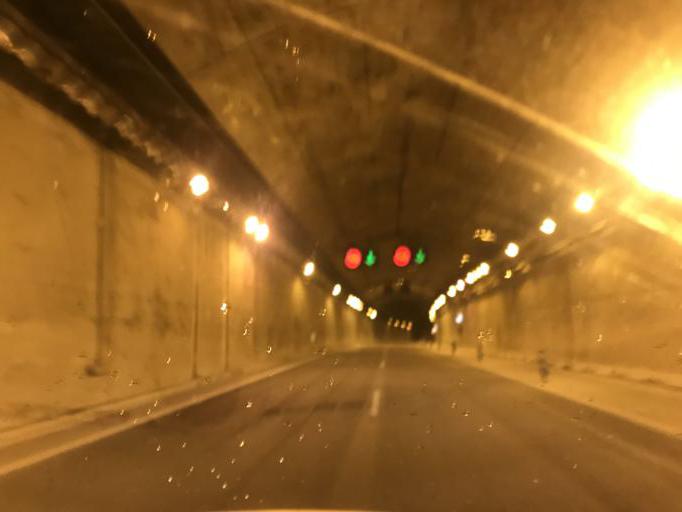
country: ES
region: Madrid
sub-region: Provincia de Madrid
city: Paracuellos de Jarama
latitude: 40.4943
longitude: -3.5552
